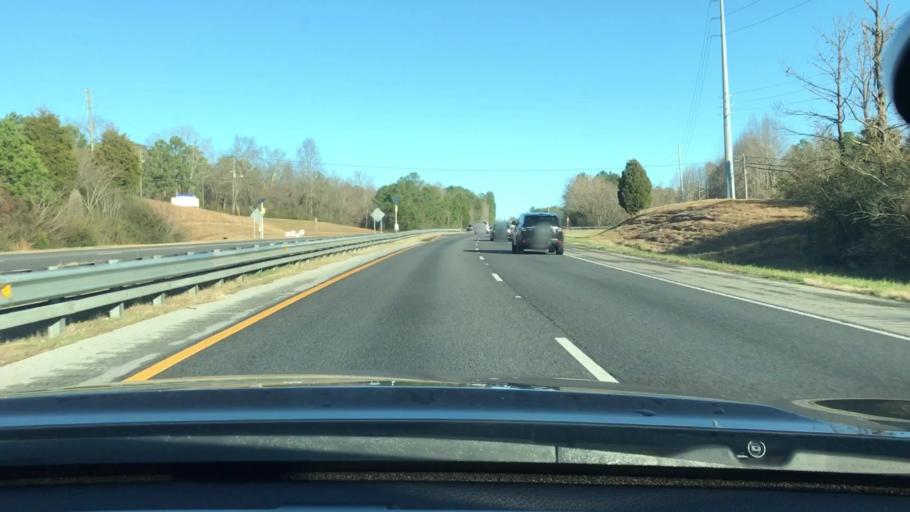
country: US
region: Alabama
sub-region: Shelby County
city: Meadowbrook
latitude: 33.3758
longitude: -86.6664
